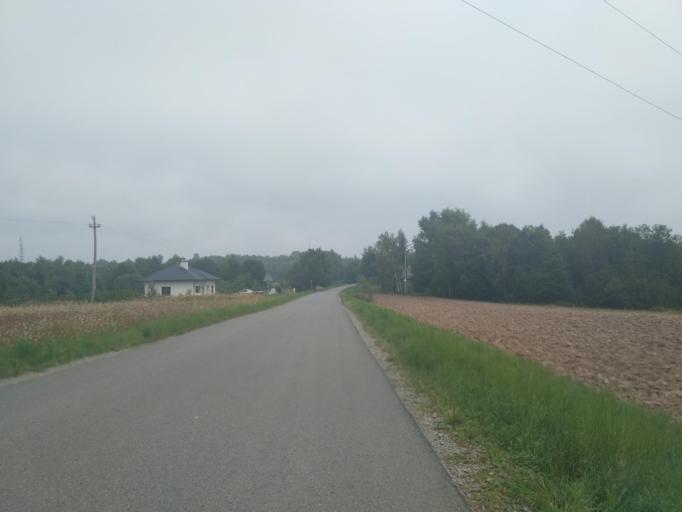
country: PL
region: Subcarpathian Voivodeship
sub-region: Powiat rzeszowski
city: Chmielnik
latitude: 50.0051
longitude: 22.1214
